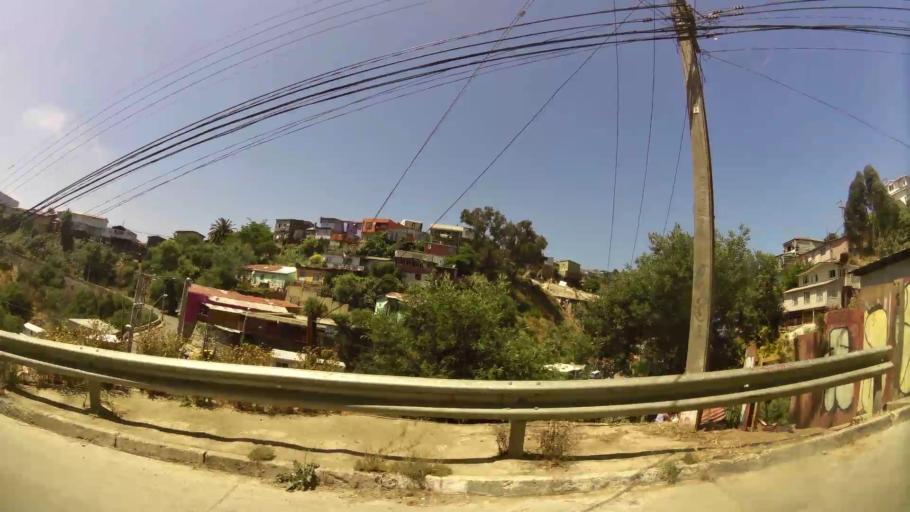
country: CL
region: Valparaiso
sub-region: Provincia de Valparaiso
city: Valparaiso
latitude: -33.0401
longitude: -71.6384
